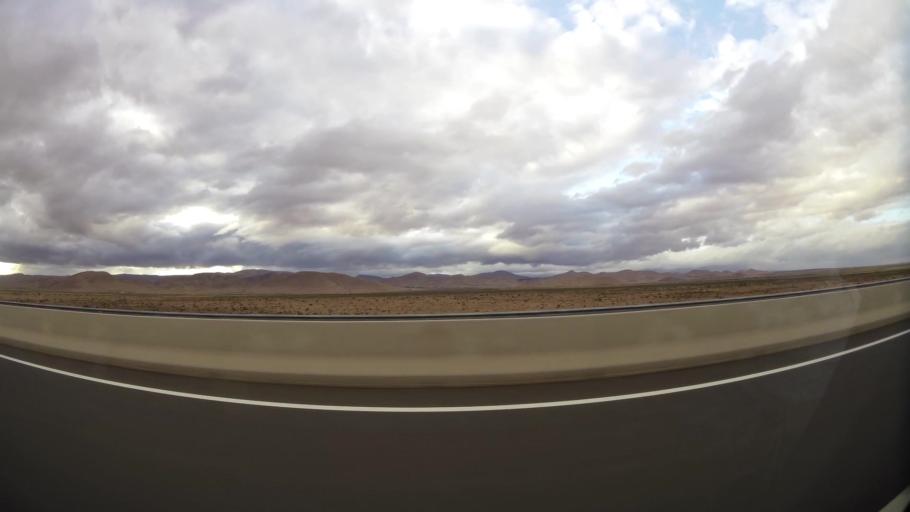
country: MA
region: Taza-Al Hoceima-Taounate
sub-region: Taza
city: Guercif
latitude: 34.3277
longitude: -3.5465
